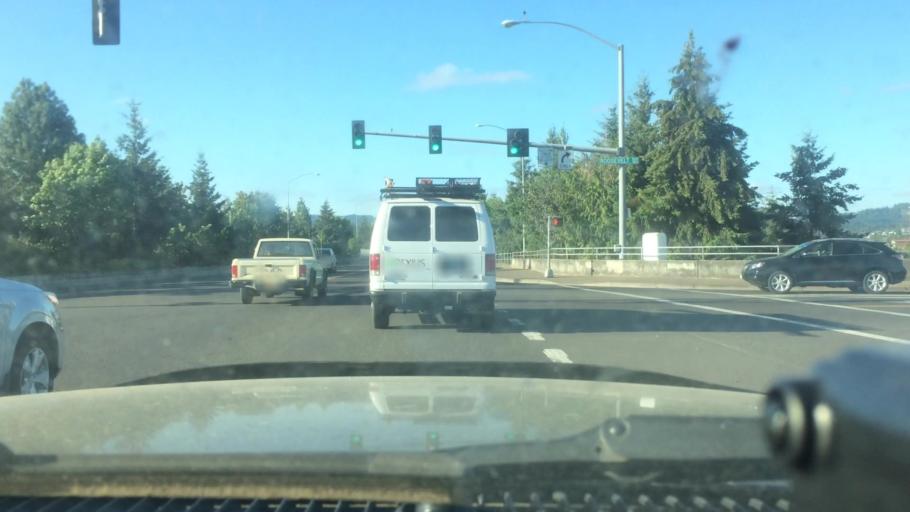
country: US
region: Oregon
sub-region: Lane County
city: Eugene
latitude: 44.0622
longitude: -123.1175
